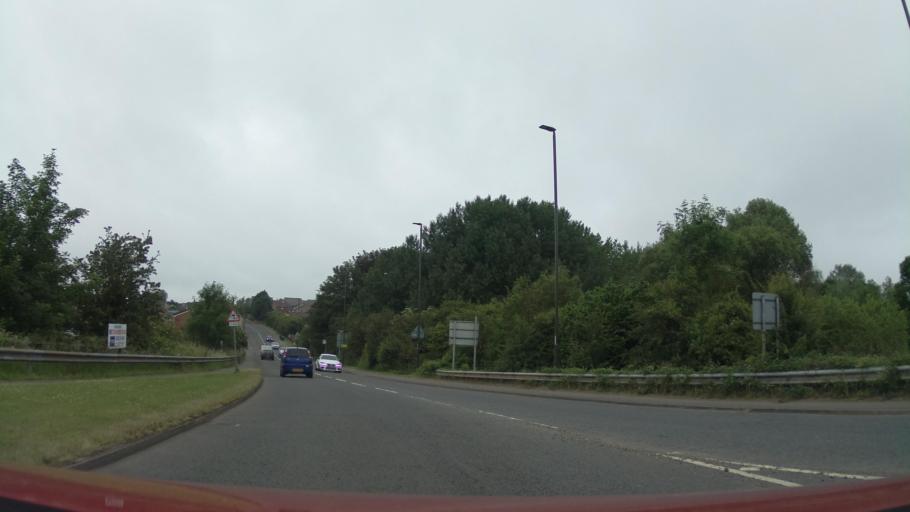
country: GB
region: England
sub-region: Derbyshire
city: Swadlincote
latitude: 52.7574
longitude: -1.5823
